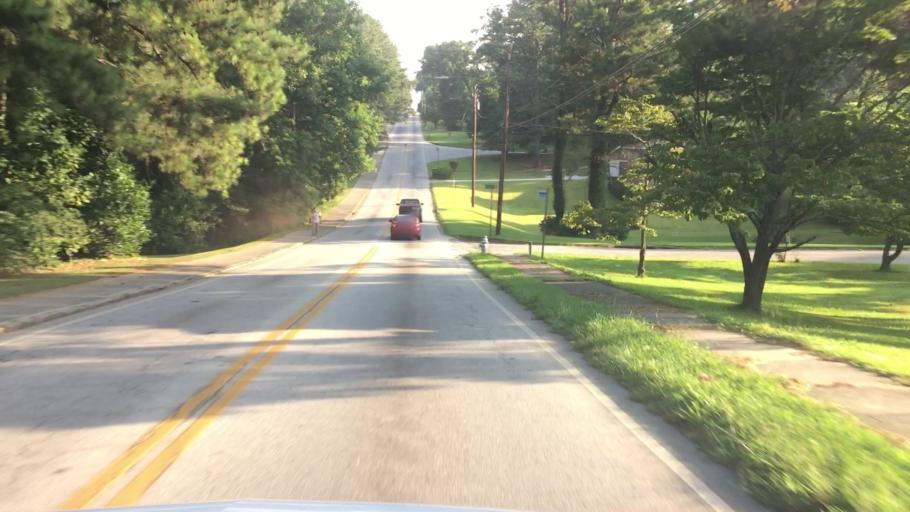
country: US
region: Georgia
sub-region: DeKalb County
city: Panthersville
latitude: 33.7044
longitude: -84.2526
